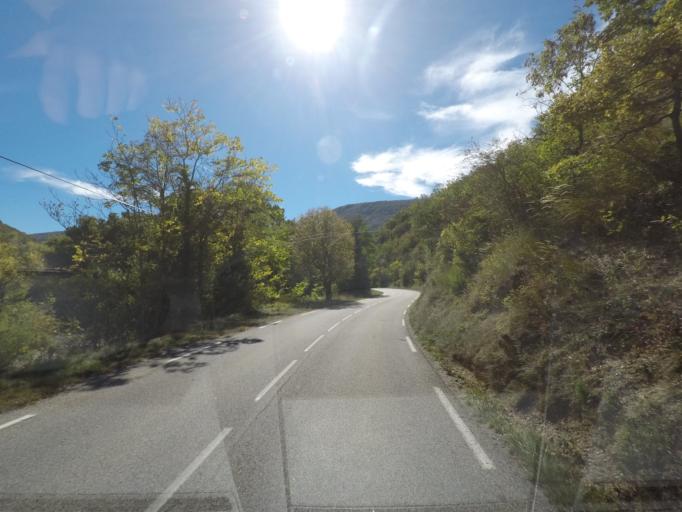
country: FR
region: Rhone-Alpes
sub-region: Departement de la Drome
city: Buis-les-Baronnies
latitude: 44.4065
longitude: 5.3501
